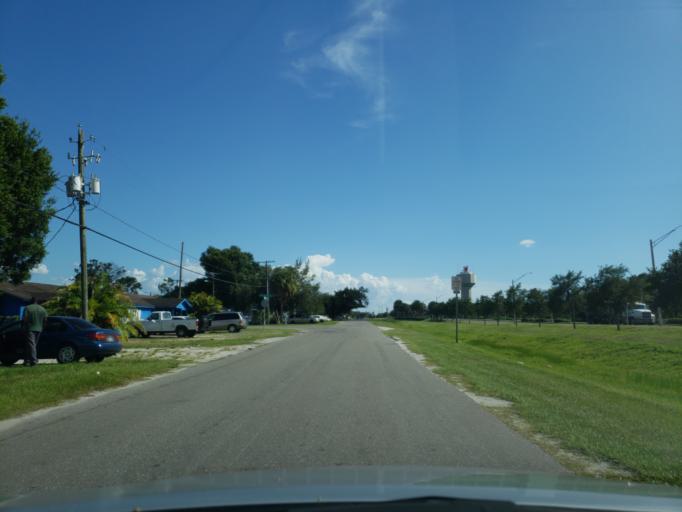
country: US
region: Florida
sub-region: Hillsborough County
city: Egypt Lake-Leto
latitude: 27.9913
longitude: -82.5195
